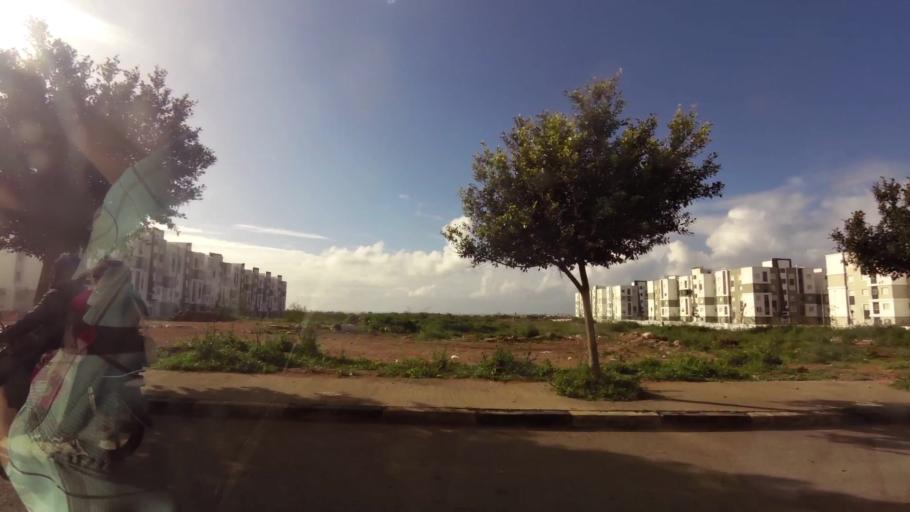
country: MA
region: Grand Casablanca
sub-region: Casablanca
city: Casablanca
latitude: 33.5510
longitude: -7.7059
